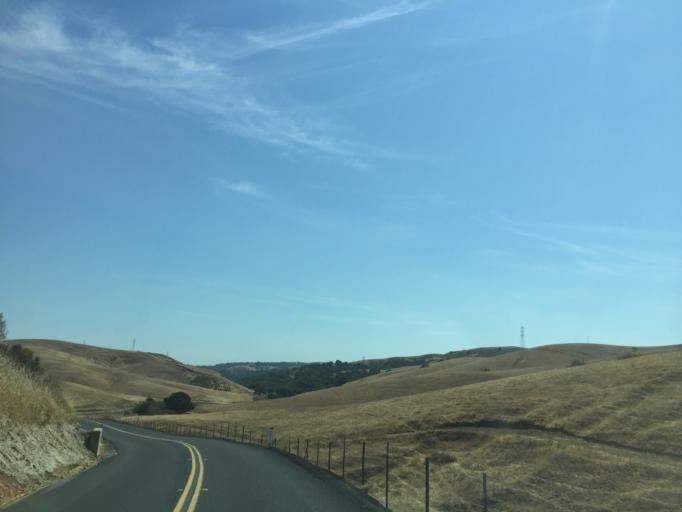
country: US
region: California
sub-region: Solano County
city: Benicia
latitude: 38.0232
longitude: -122.1818
